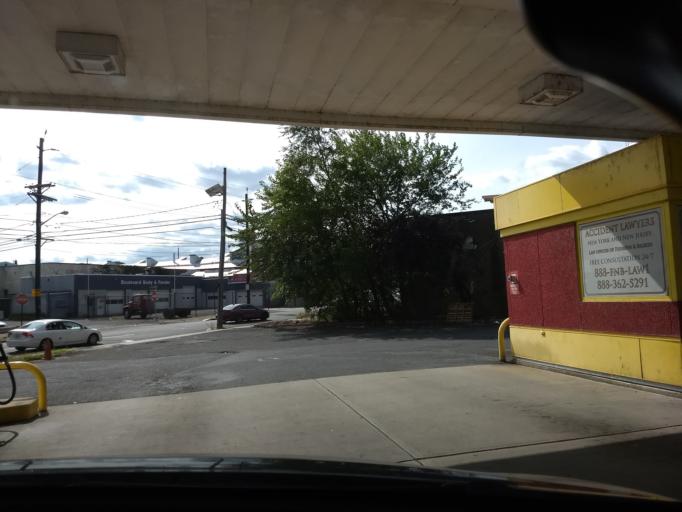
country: US
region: New Jersey
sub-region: Passaic County
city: Hawthorne
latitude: 40.9404
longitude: -74.1446
